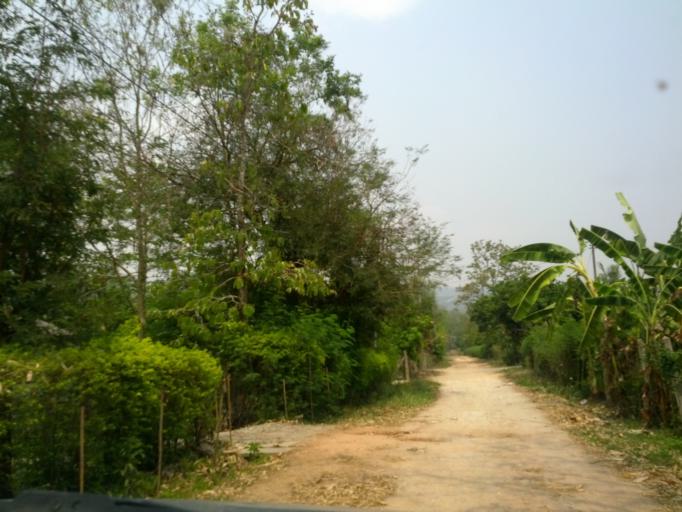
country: TH
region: Chiang Mai
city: San Sai
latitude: 18.9335
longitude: 99.0347
